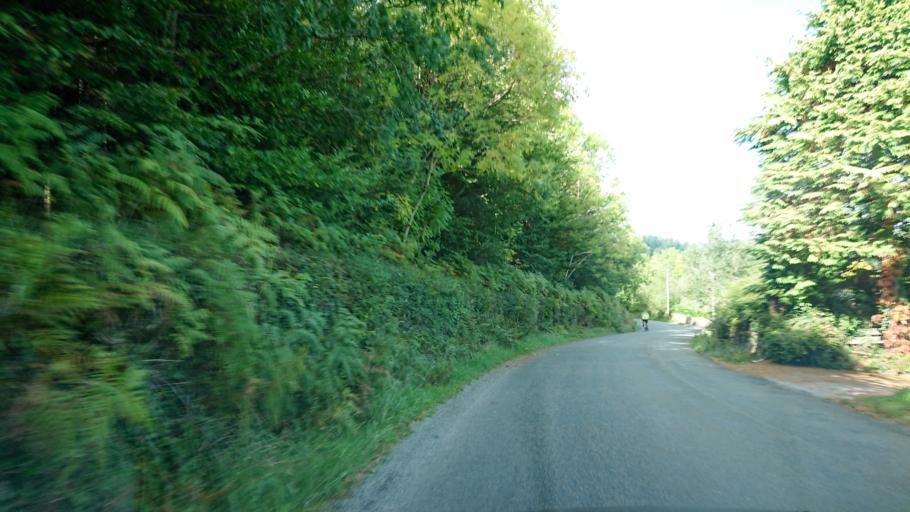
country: IE
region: Munster
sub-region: Waterford
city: Dungarvan
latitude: 52.1206
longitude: -7.6876
